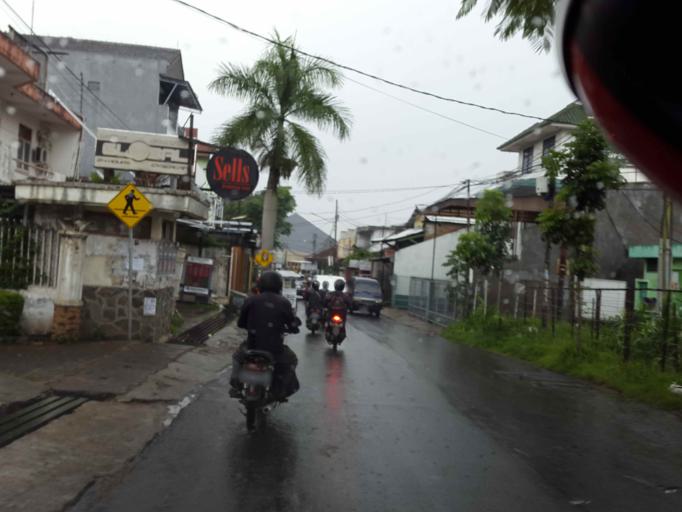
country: ID
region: West Java
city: Cimahi
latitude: -6.8799
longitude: 107.5587
